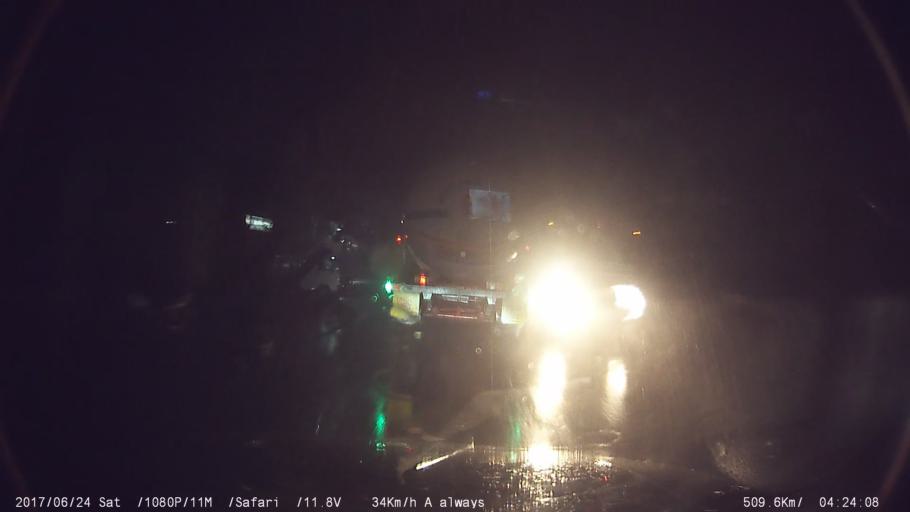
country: IN
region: Kerala
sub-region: Ernakulam
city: Cochin
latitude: 9.9854
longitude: 76.3521
